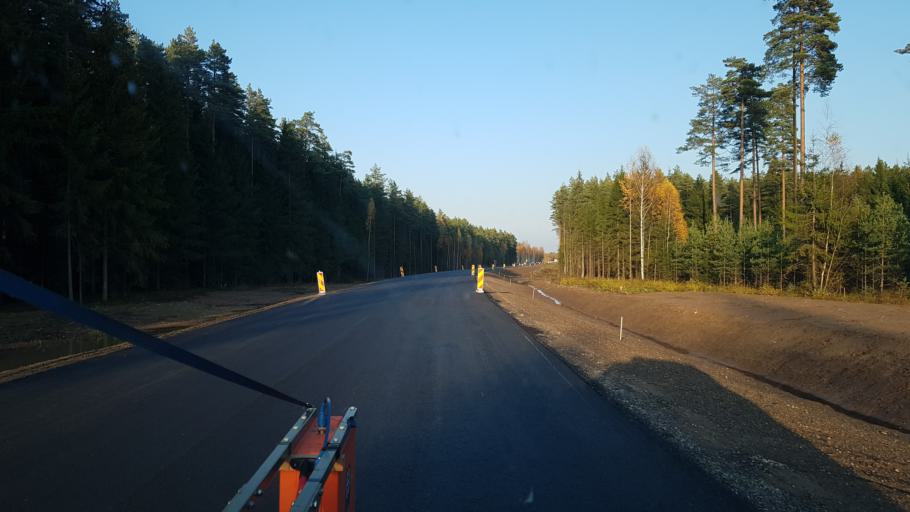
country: EE
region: Polvamaa
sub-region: Polva linn
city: Polva
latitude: 57.9348
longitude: 27.1888
